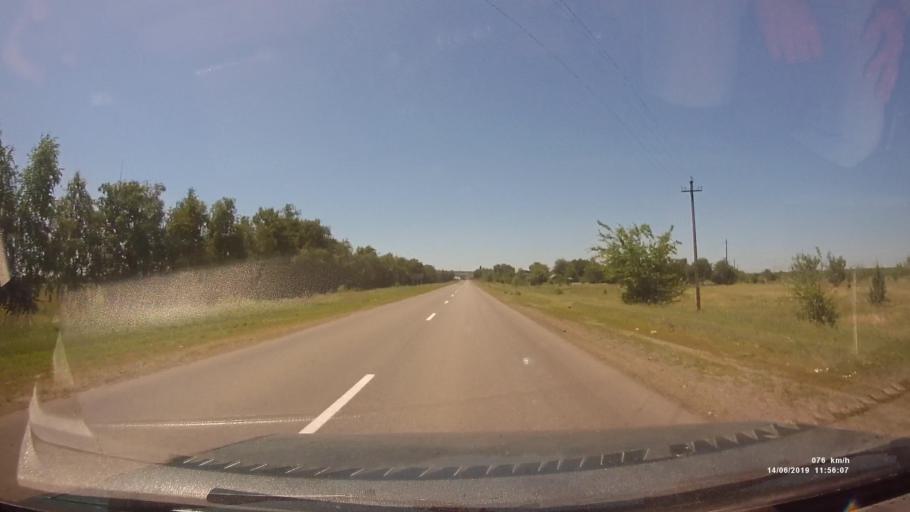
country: RU
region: Rostov
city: Kazanskaya
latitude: 49.8051
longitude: 41.1657
